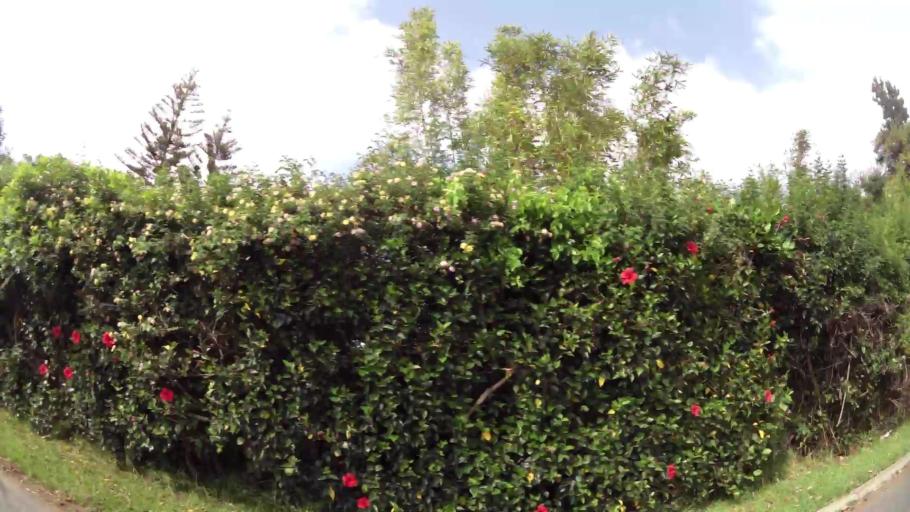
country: MA
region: Rabat-Sale-Zemmour-Zaer
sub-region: Rabat
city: Rabat
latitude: 33.9736
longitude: -6.8522
